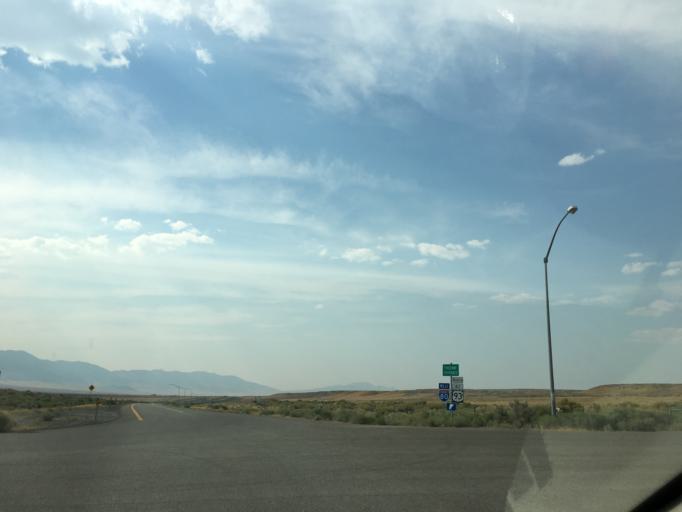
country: US
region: Nevada
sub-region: Elko County
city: West Wendover
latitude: 40.7531
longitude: -114.1129
